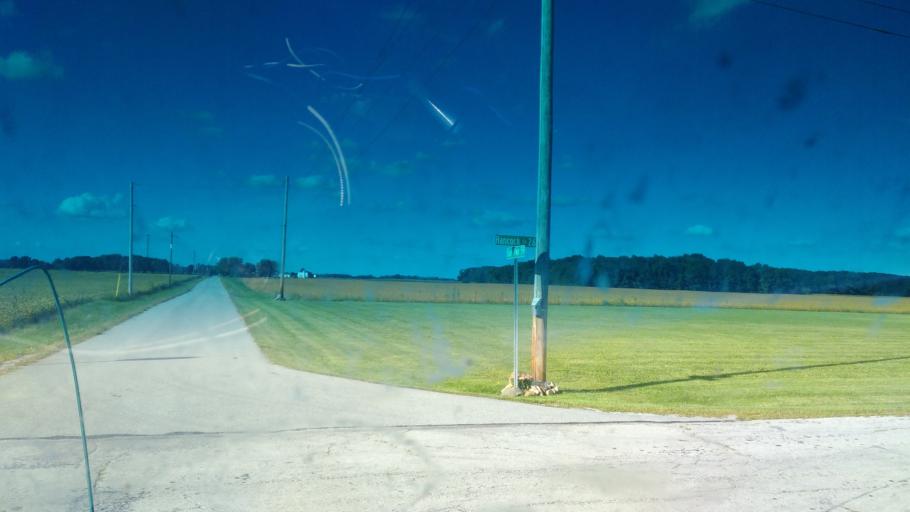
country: US
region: Ohio
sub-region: Hancock County
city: Arlington
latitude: 40.9364
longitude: -83.7657
